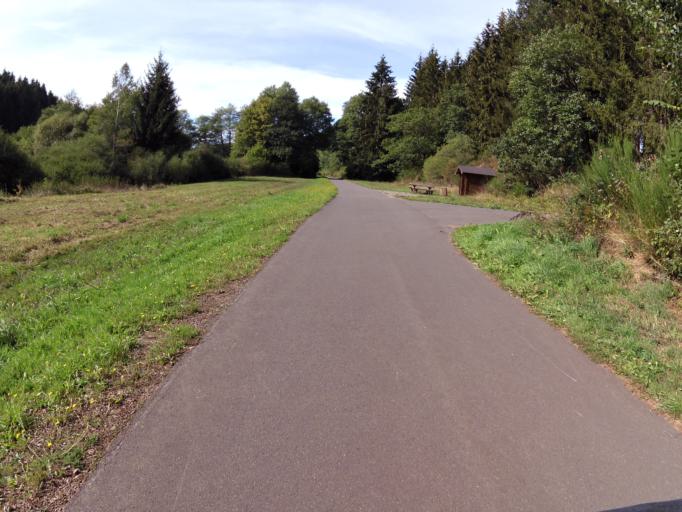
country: DE
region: Rheinland-Pfalz
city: Pronsfeld
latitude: 50.1850
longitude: 6.3099
